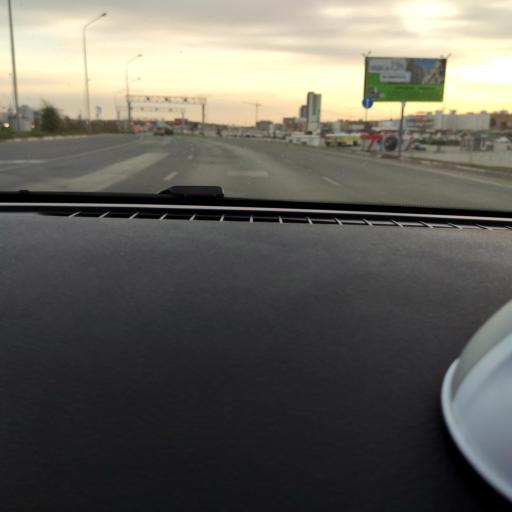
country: RU
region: Samara
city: Samara
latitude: 53.1431
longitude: 50.1786
